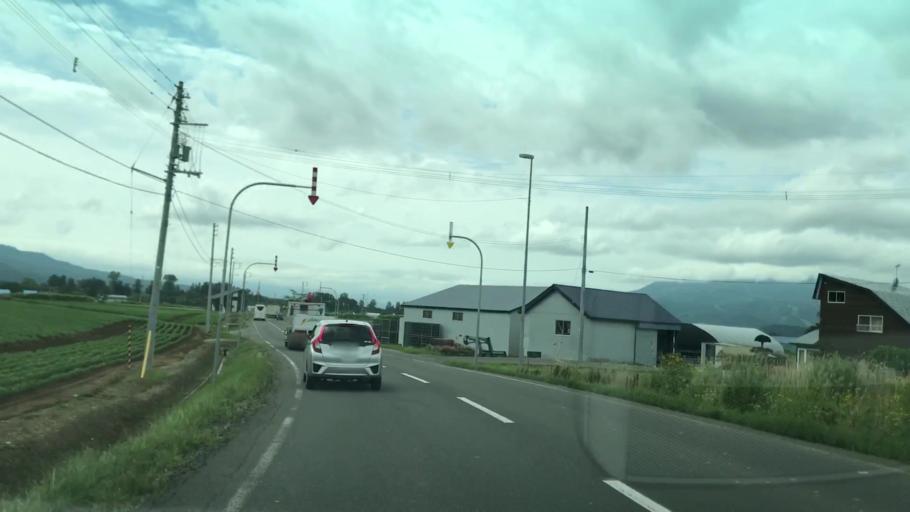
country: JP
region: Hokkaido
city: Niseko Town
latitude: 42.9343
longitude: 140.8040
